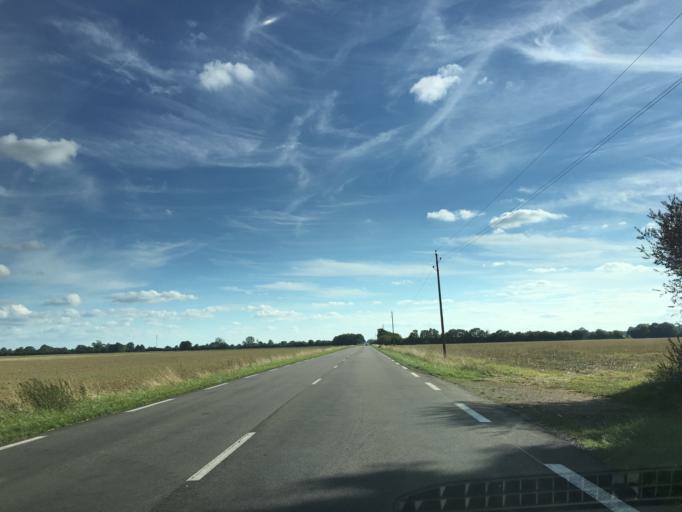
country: FR
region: Lower Normandy
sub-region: Departement du Calvados
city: Orbec
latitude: 48.9393
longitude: 0.4491
